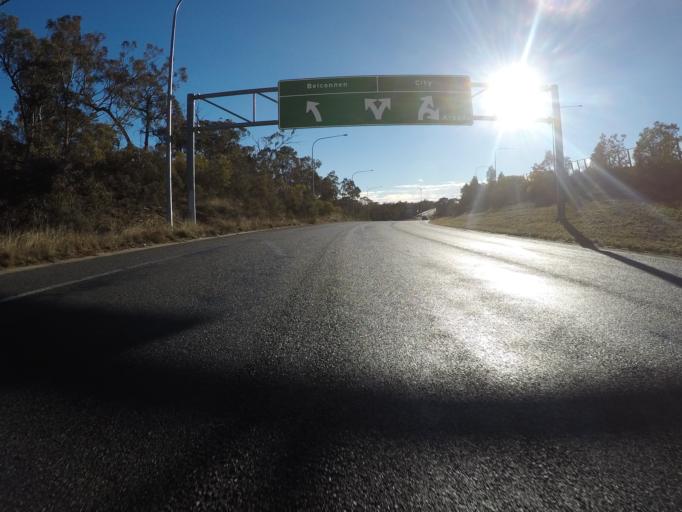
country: AU
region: Australian Capital Territory
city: Macquarie
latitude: -35.2582
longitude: 149.0878
